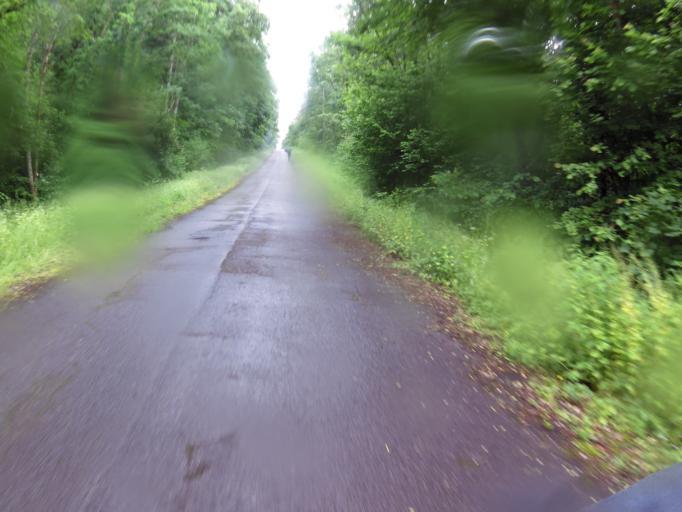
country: FR
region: Champagne-Ardenne
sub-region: Departement de la Haute-Marne
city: Chancenay
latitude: 48.7438
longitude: 4.9807
